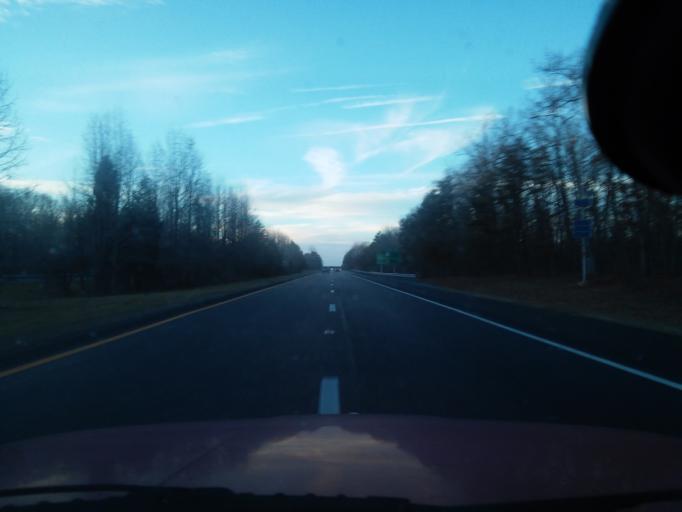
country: US
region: Virginia
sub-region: Louisa County
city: Louisa
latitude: 37.8804
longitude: -78.0260
